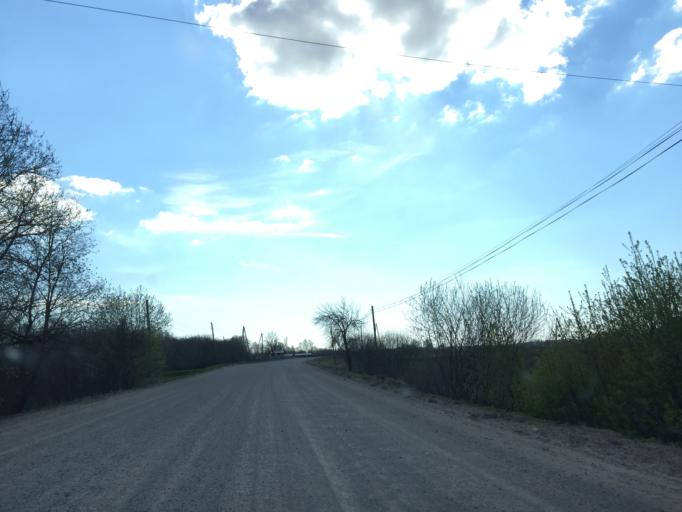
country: LV
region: Saulkrastu
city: Saulkrasti
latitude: 57.3392
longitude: 24.5213
